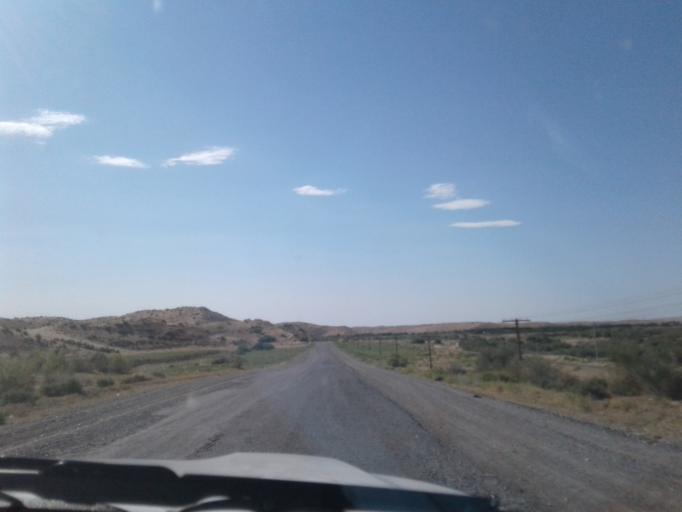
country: TM
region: Mary
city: Yoloeten
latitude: 36.5148
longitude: 62.5613
